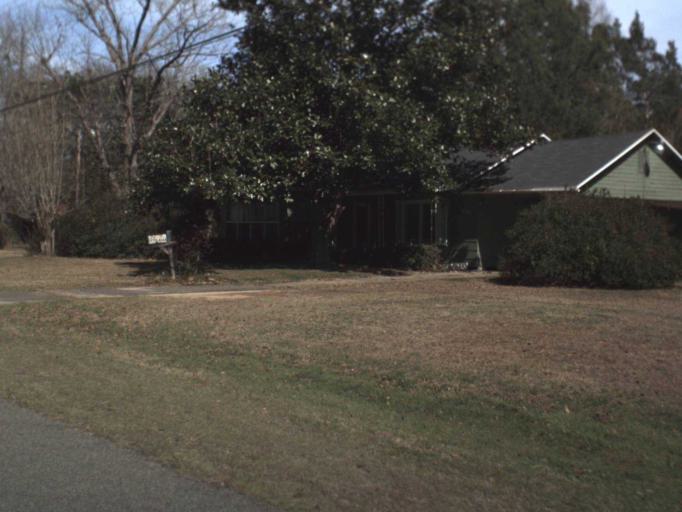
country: US
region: Florida
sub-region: Jackson County
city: Graceville
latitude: 30.8693
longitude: -85.5266
